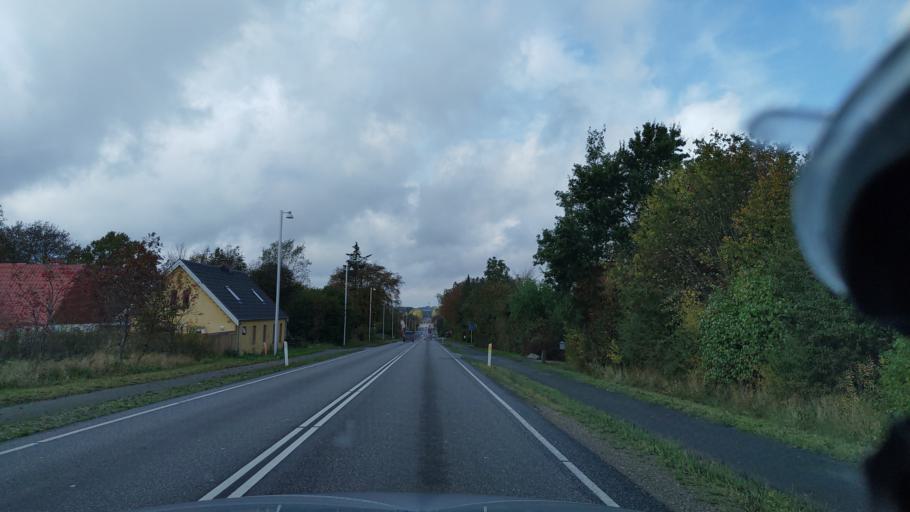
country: DK
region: Zealand
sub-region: Naestved Kommune
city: Fensmark
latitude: 55.2581
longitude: 11.8825
